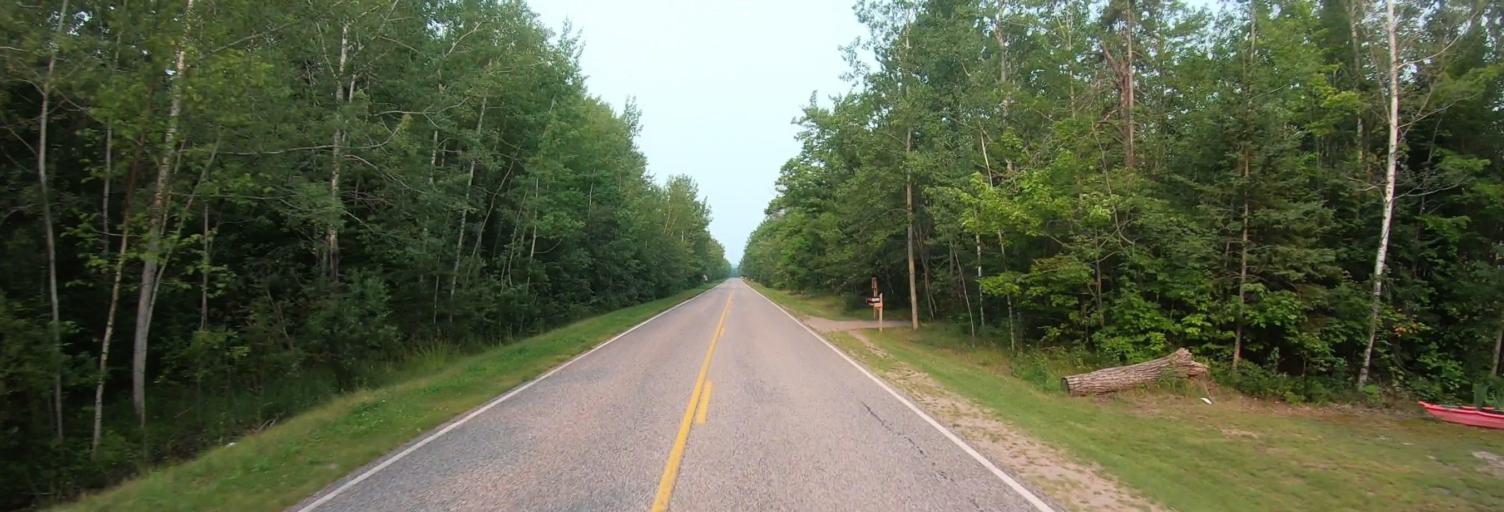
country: US
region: Michigan
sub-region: Chippewa County
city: Sault Ste. Marie
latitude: 46.4657
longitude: -84.8771
